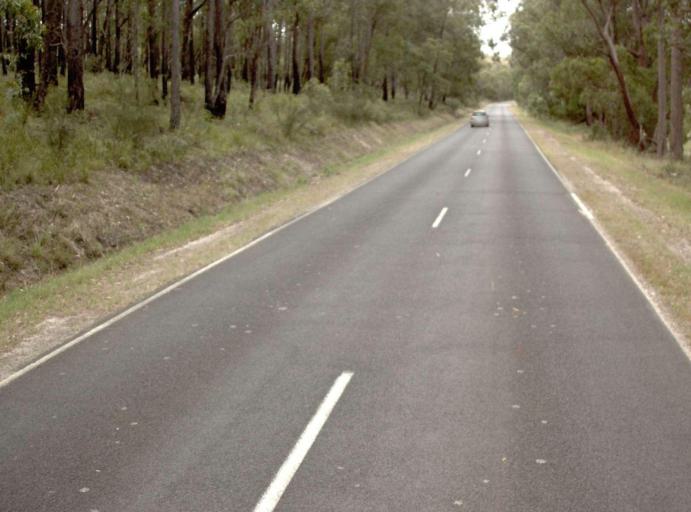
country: AU
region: Victoria
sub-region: Latrobe
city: Traralgon
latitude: -38.4248
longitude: 146.8183
